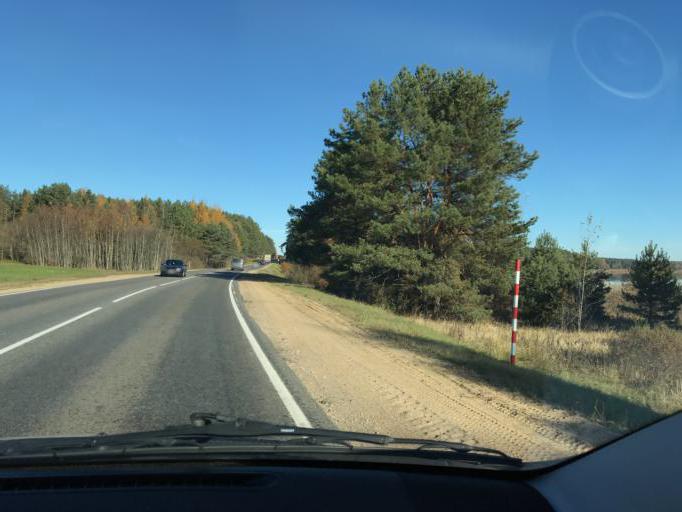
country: BY
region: Vitebsk
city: Polatsk
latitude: 55.3151
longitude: 28.7764
